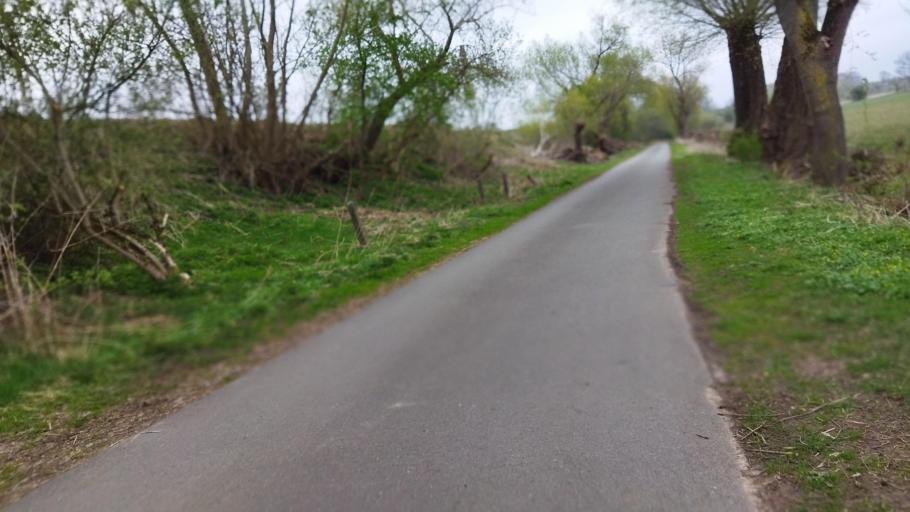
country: DE
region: Lower Saxony
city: Riede
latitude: 53.0275
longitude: 8.8864
